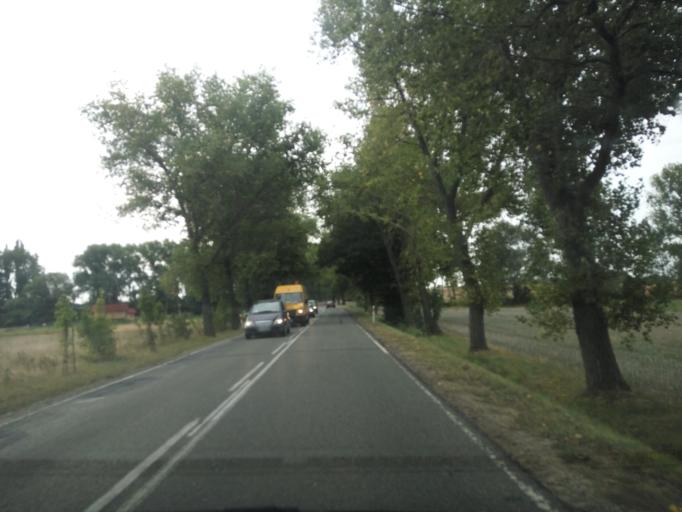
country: PL
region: Lower Silesian Voivodeship
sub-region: Powiat strzelinski
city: Strzelin
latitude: 50.8078
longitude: 17.0608
